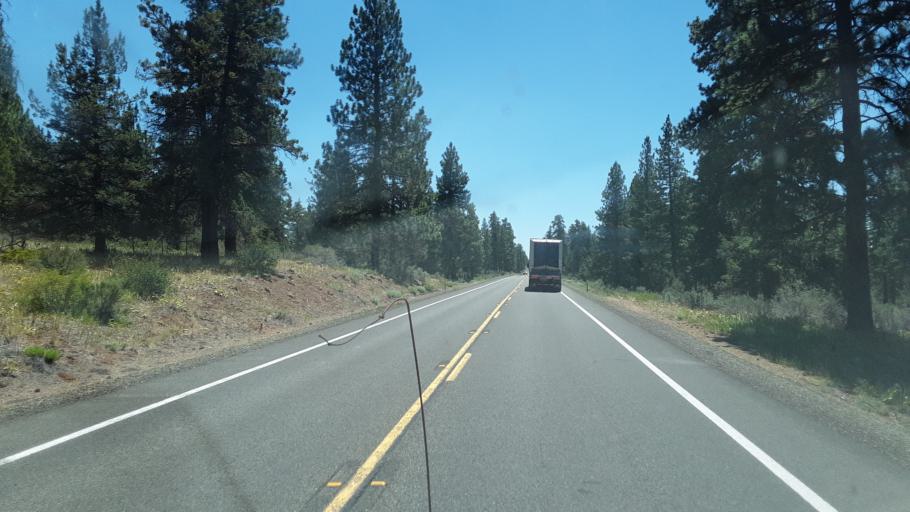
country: US
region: California
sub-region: Siskiyou County
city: Tulelake
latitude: 41.5689
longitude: -121.1785
